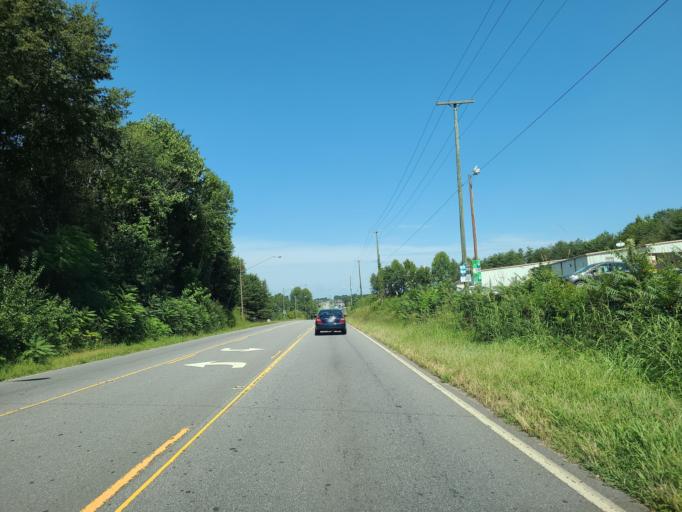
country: US
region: North Carolina
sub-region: Lincoln County
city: Lincolnton
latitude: 35.4805
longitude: -81.2416
